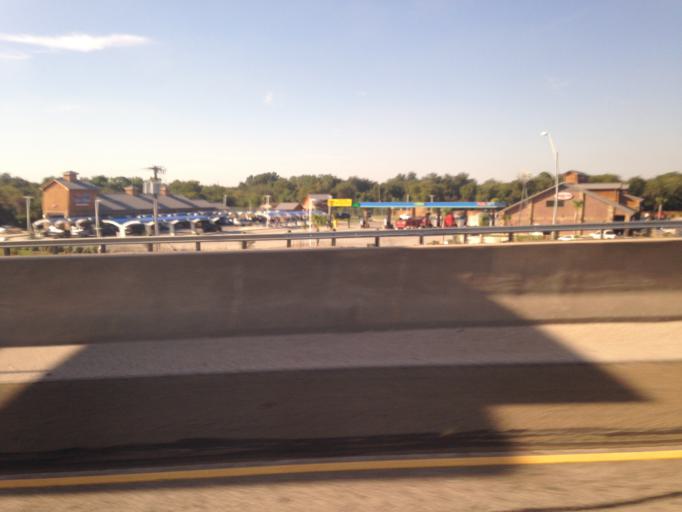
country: US
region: Texas
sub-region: Tarrant County
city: Haltom City
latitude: 32.7806
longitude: -97.2754
